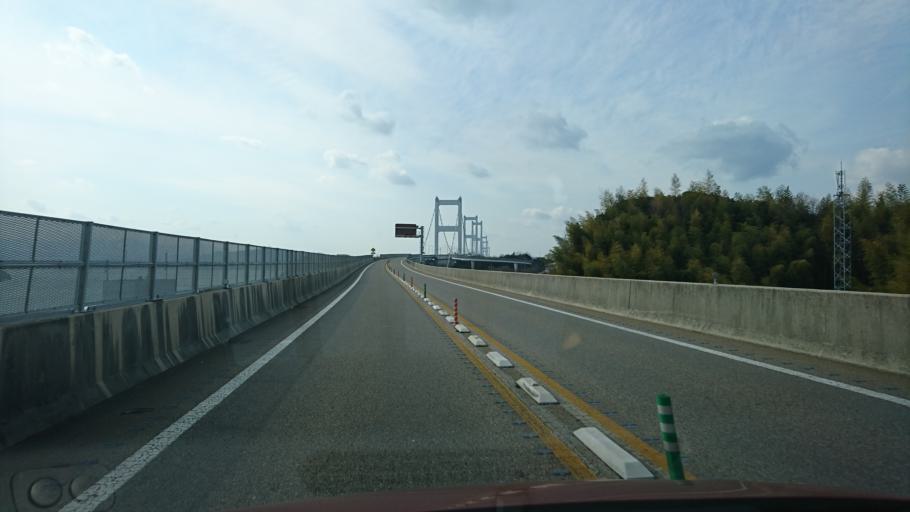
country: JP
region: Hiroshima
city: Innoshima
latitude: 34.1298
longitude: 133.0215
